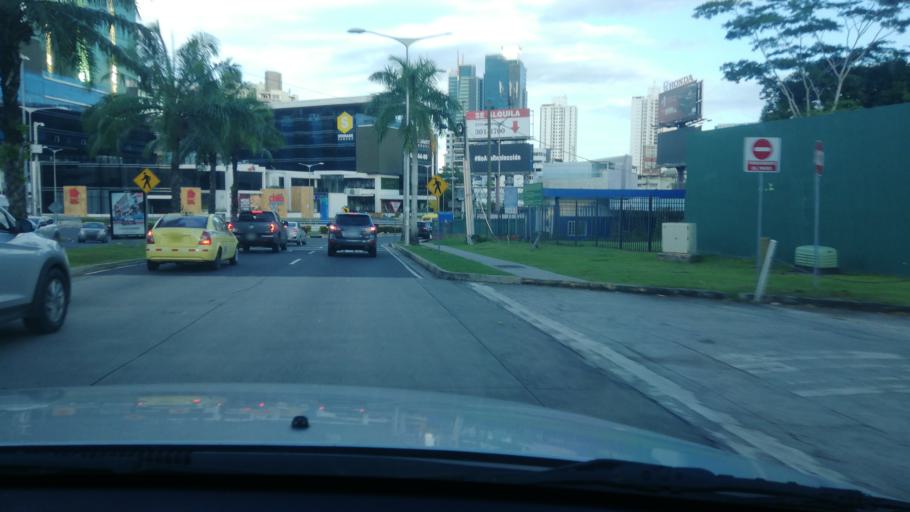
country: PA
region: Panama
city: Panama
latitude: 8.9838
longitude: -79.5124
